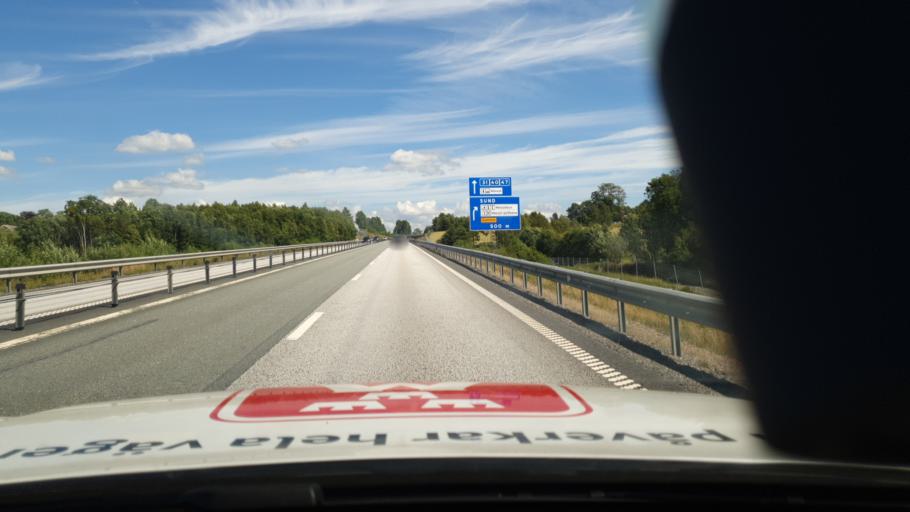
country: SE
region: Joenkoeping
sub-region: Nassjo Kommun
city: Nassjo
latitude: 57.6822
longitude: 14.6590
